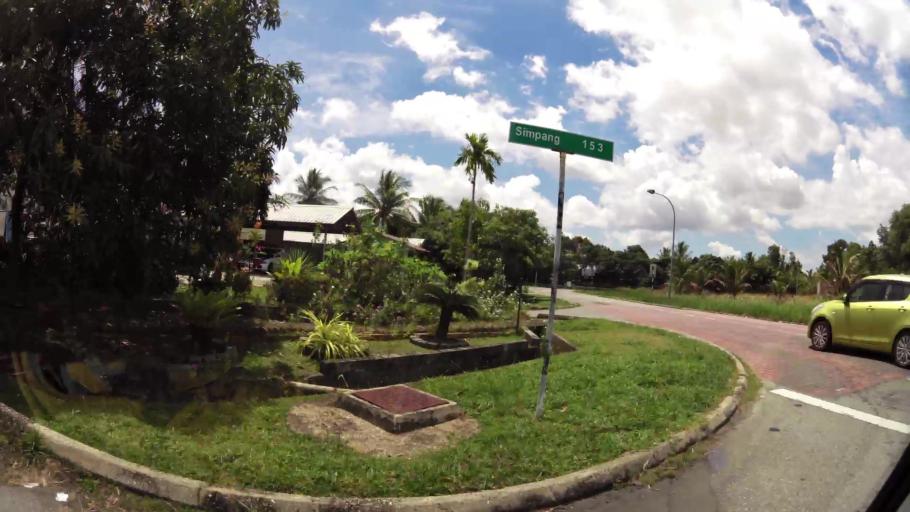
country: BN
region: Brunei and Muara
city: Bandar Seri Begawan
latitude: 4.9607
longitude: 114.9030
